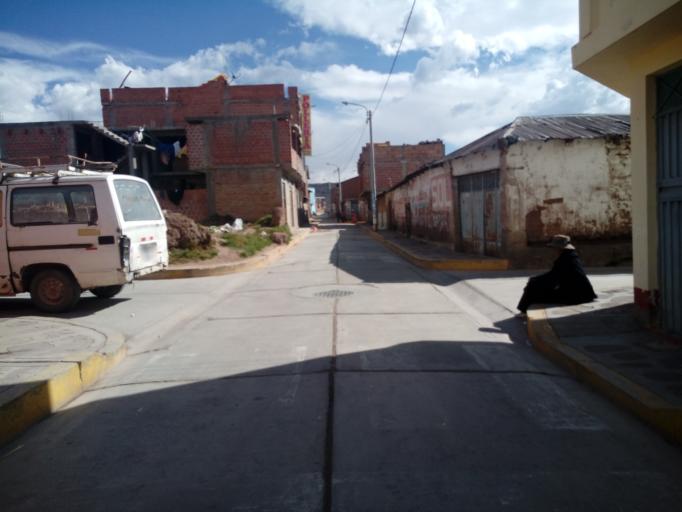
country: PE
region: Puno
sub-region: Provincia de Chucuito
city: Zepita
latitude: -16.4960
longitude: -69.1034
